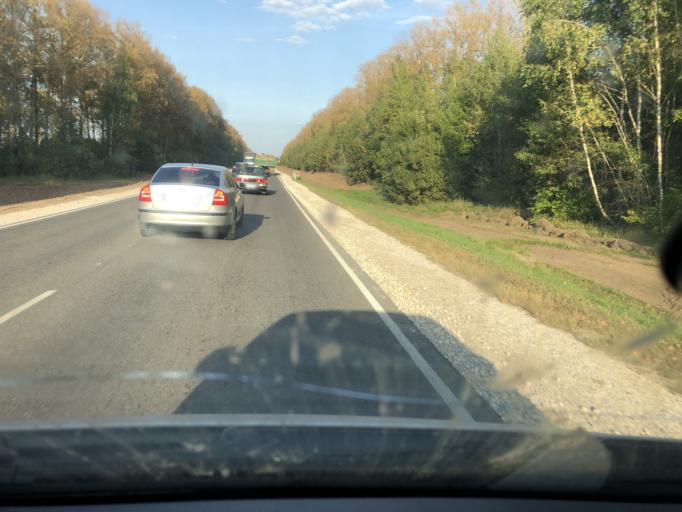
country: RU
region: Kaluga
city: Peremyshl'
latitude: 54.2511
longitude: 36.1112
